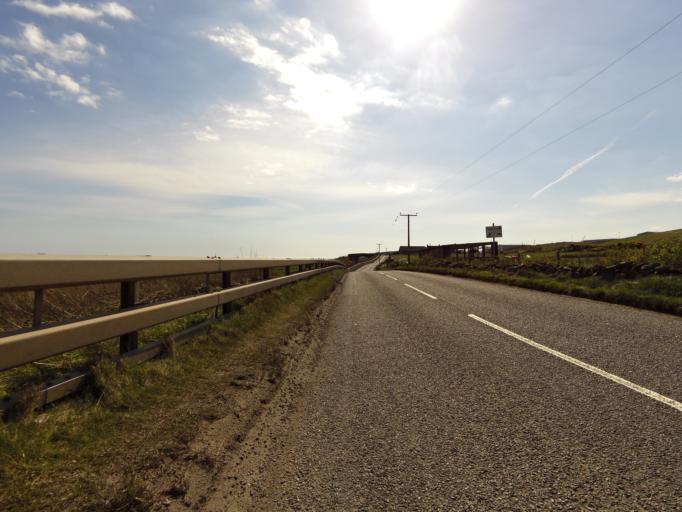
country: GB
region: Scotland
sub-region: Aberdeen City
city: Aberdeen
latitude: 57.1240
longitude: -2.0558
